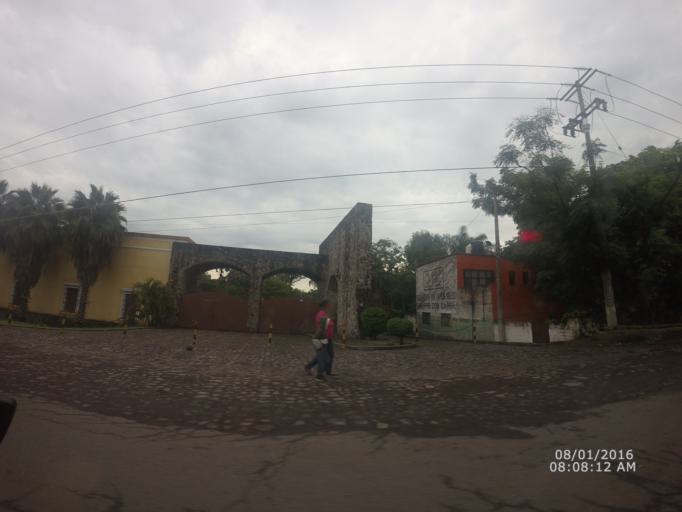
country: MX
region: Nayarit
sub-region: Tepic
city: La Corregidora
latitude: 21.4526
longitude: -104.8185
